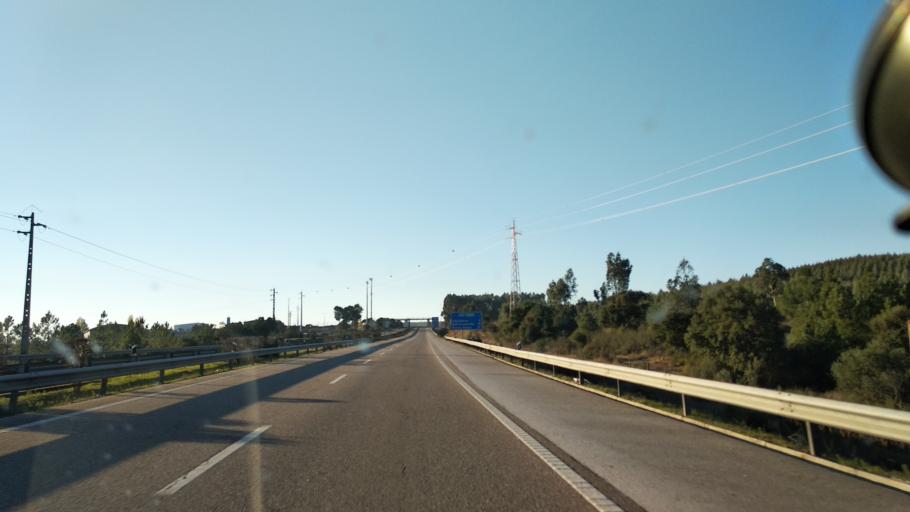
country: PT
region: Santarem
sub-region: Abrantes
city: Tramagal
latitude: 39.4869
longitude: -8.2822
